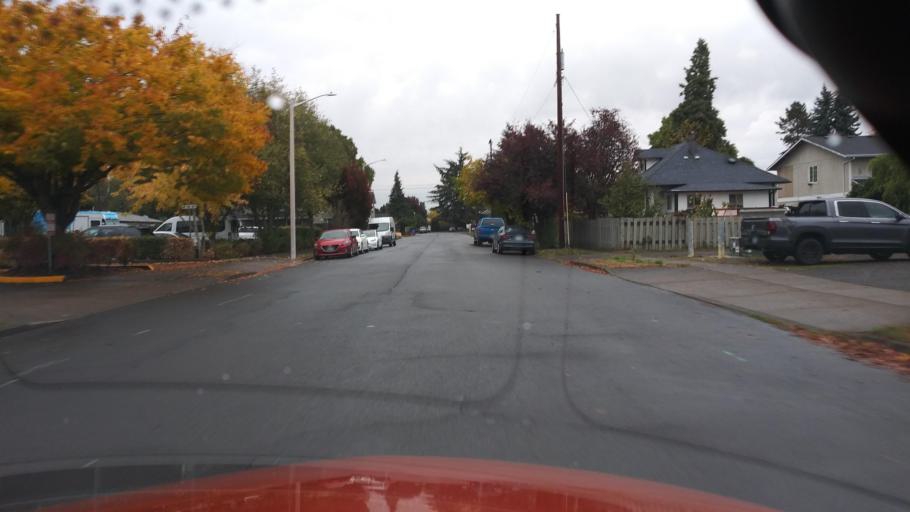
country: US
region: Oregon
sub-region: Washington County
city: Cornelius
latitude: 45.5211
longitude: -123.0571
